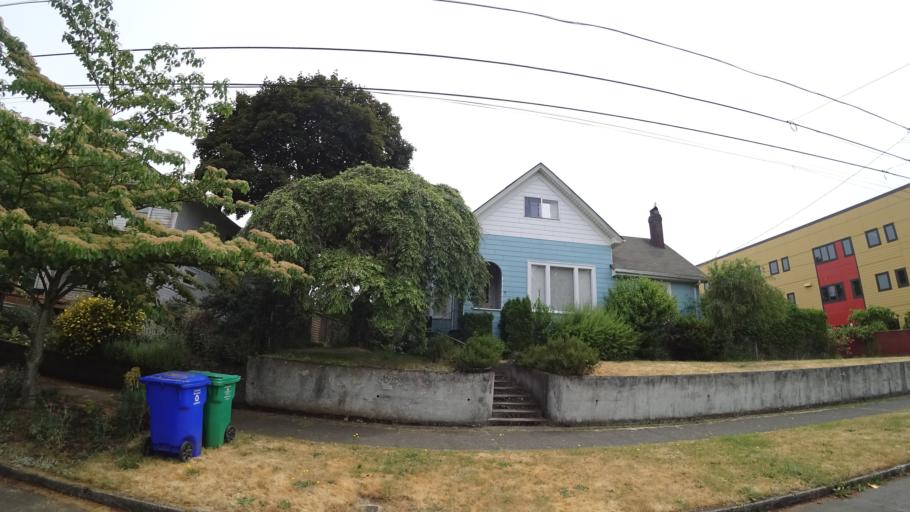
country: US
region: Oregon
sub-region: Multnomah County
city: Portland
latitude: 45.5634
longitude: -122.6936
